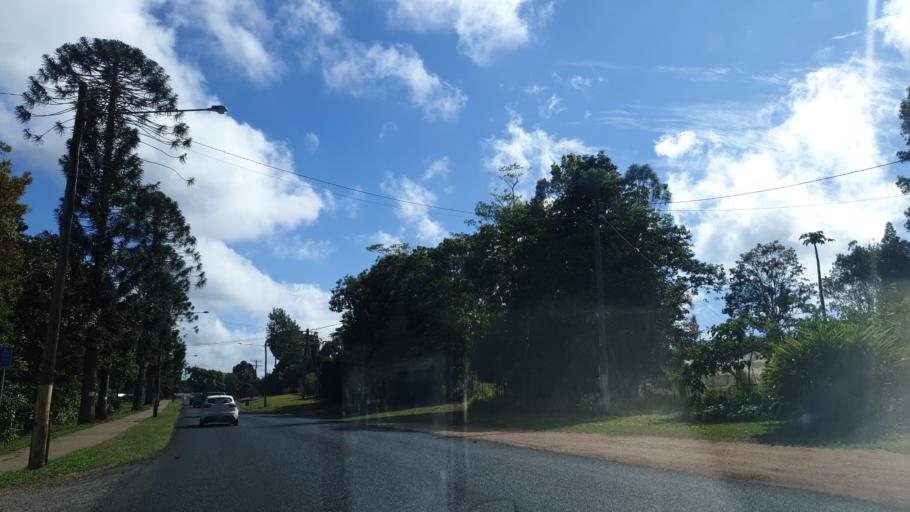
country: AU
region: Queensland
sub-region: Tablelands
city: Atherton
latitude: -17.3539
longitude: 145.5882
